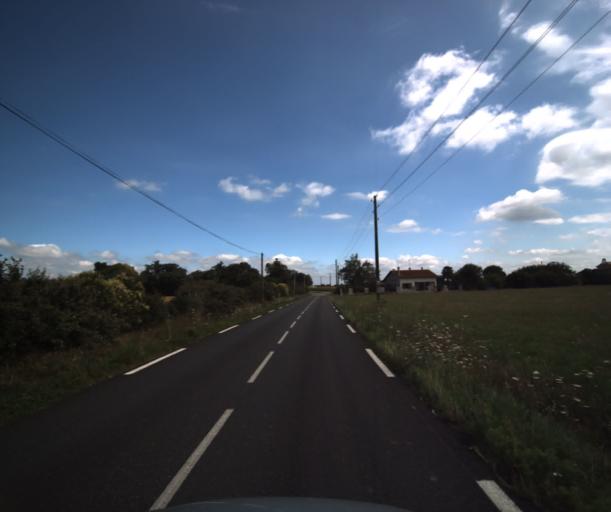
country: FR
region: Midi-Pyrenees
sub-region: Departement de la Haute-Garonne
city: Lacasse
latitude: 43.3845
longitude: 1.2477
